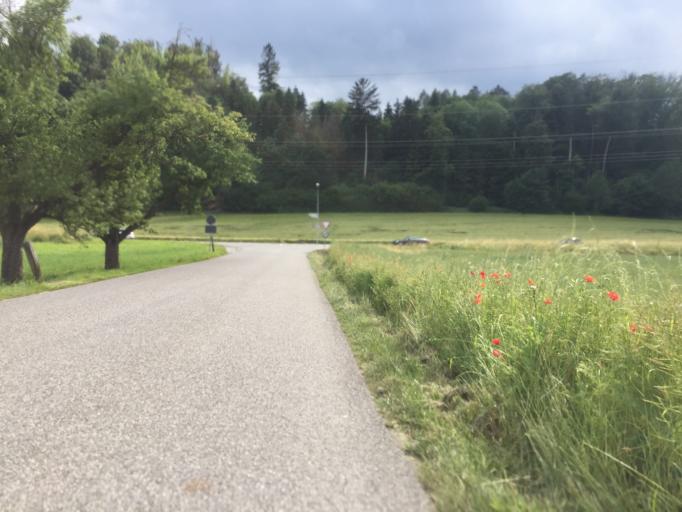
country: CH
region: Bern
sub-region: Bern-Mittelland District
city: Stettlen
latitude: 46.9593
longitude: 7.5107
